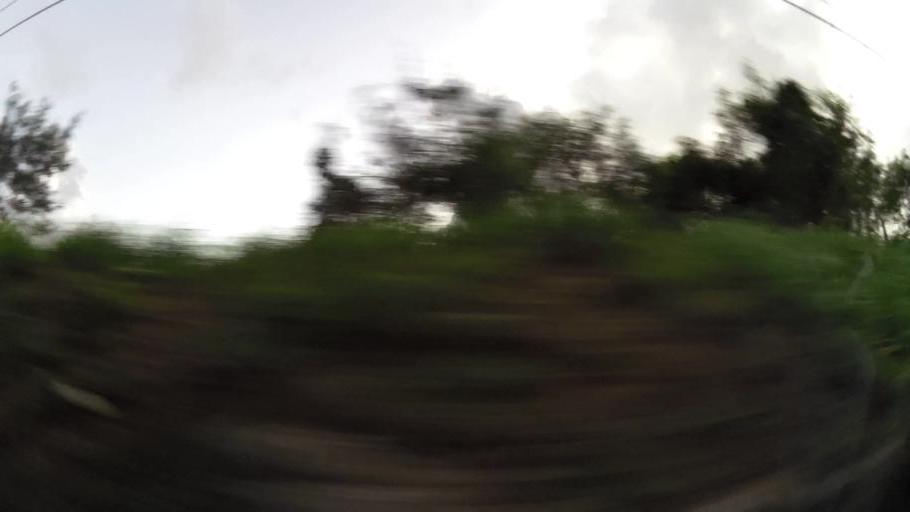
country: BB
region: Saint John
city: Four Cross Roads
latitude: 13.1186
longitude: -59.5044
